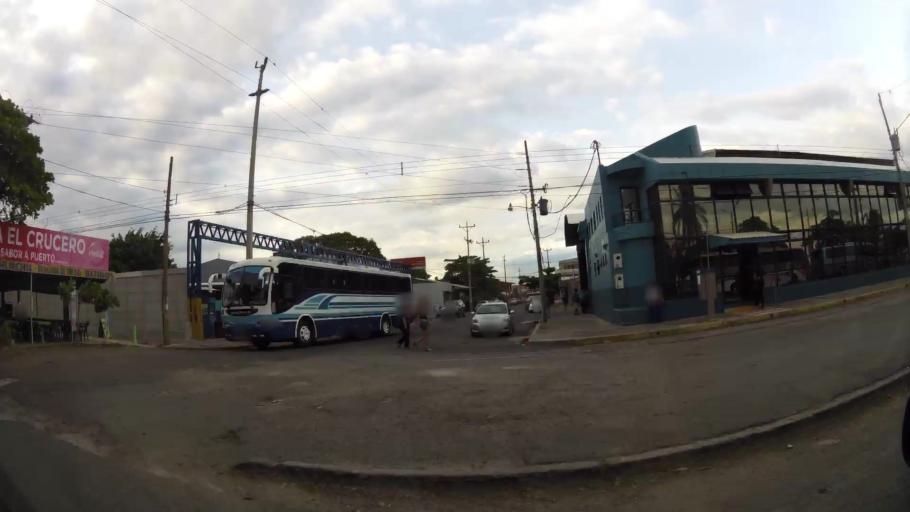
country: CR
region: Puntarenas
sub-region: Canton Central de Puntarenas
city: Puntarenas
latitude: 9.9757
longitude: -84.8305
